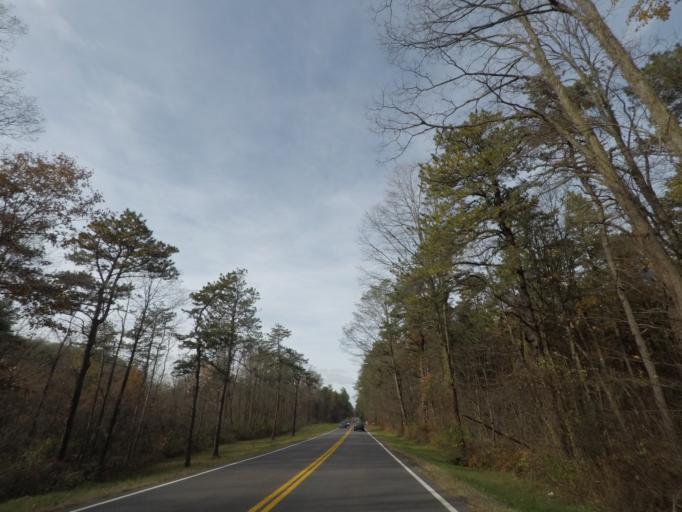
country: US
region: New York
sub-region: Albany County
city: Westmere
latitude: 42.7250
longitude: -73.8928
